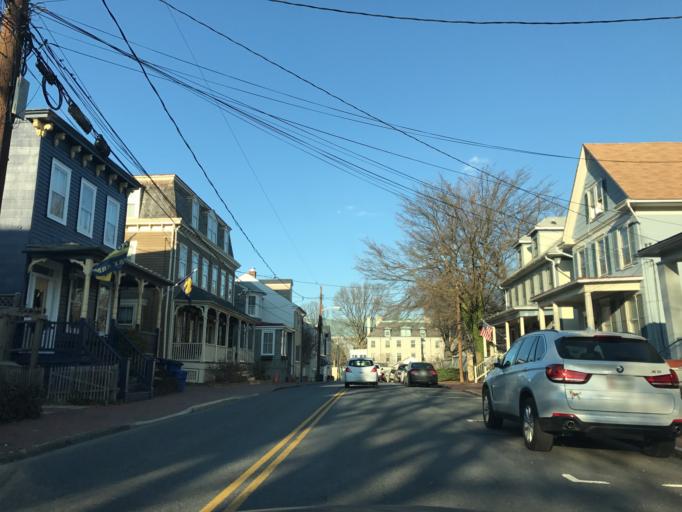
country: US
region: Maryland
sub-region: Anne Arundel County
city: Annapolis
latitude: 38.9786
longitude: -76.4863
